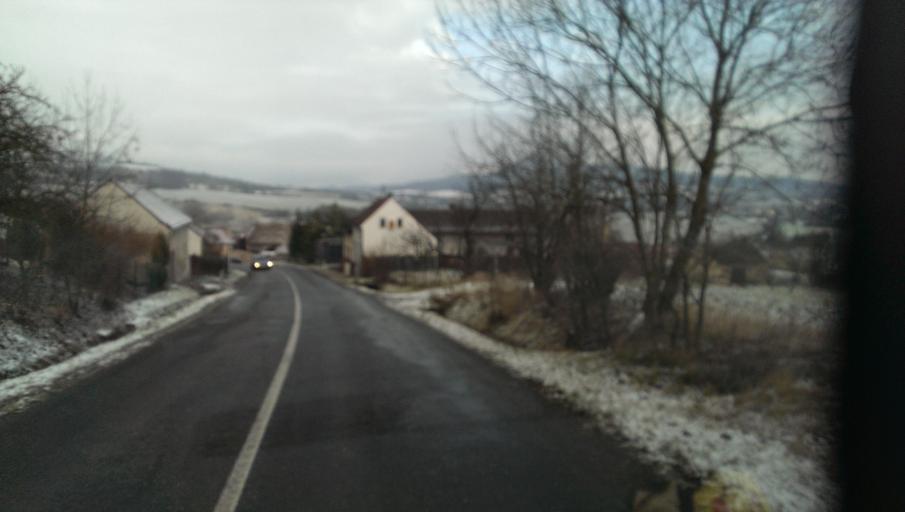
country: CZ
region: Ustecky
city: Trebenice
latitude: 50.4607
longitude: 13.9953
